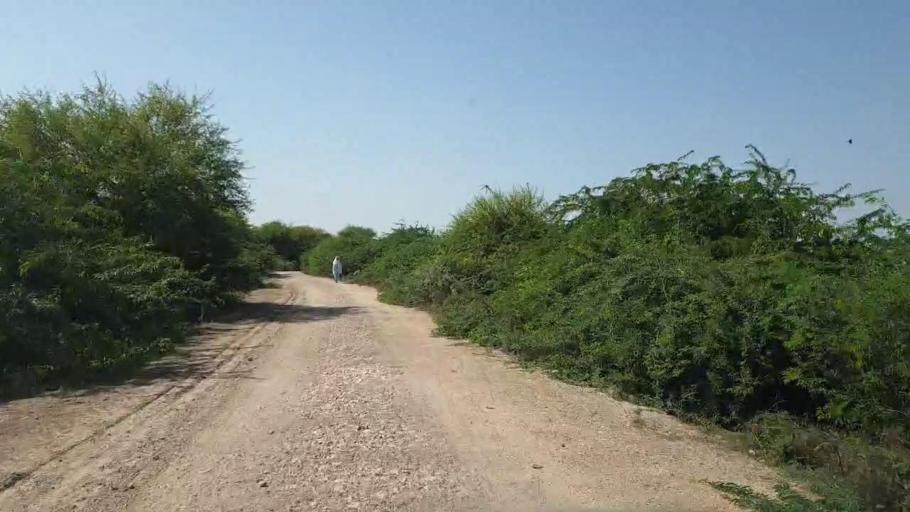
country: PK
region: Sindh
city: Tando Bago
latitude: 24.7068
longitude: 69.0470
